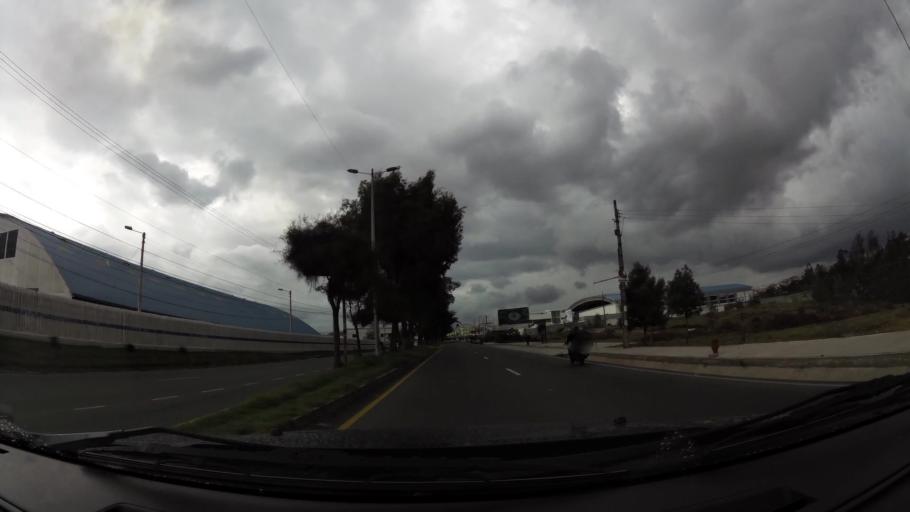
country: EC
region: Pichincha
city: Quito
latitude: -0.0722
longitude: -78.4744
